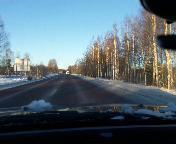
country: SE
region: Gaevleborg
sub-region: Ljusdals Kommun
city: Jaervsoe
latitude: 61.7561
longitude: 16.1611
